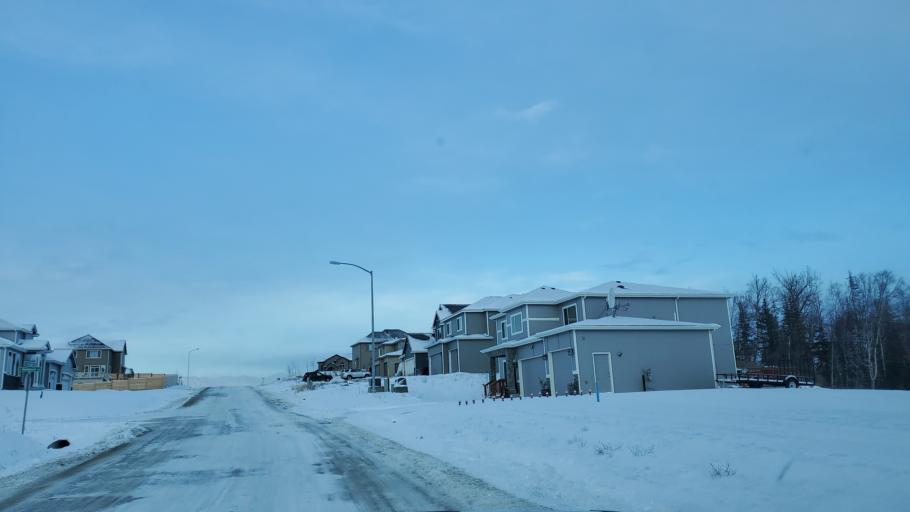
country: US
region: Alaska
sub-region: Matanuska-Susitna Borough
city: Lakes
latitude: 61.5459
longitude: -149.3184
